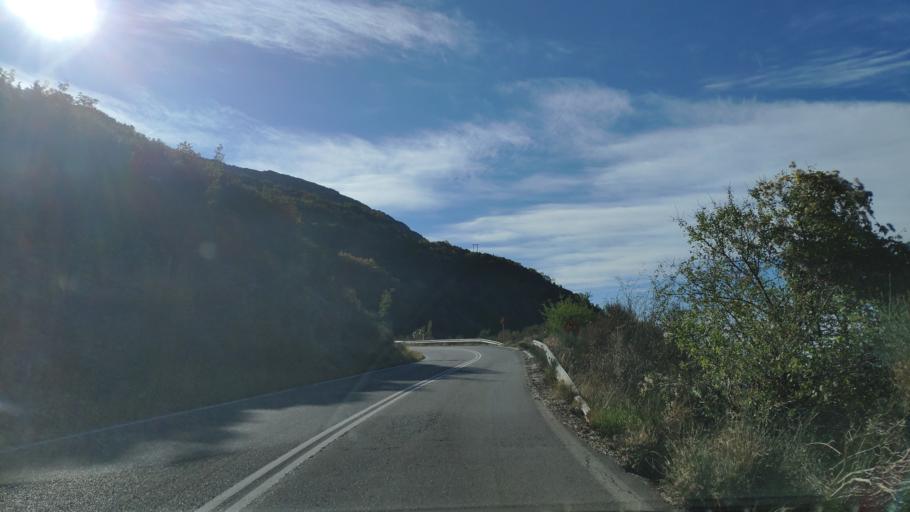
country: GR
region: Peloponnese
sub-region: Nomos Arkadias
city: Dimitsana
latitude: 37.5648
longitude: 22.0619
